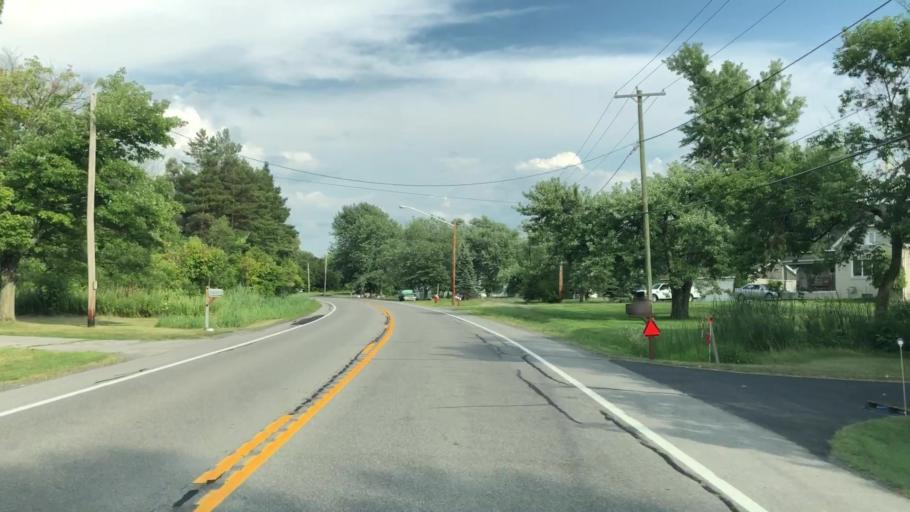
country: US
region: New York
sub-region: Erie County
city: Elma Center
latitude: 42.8559
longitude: -78.6697
